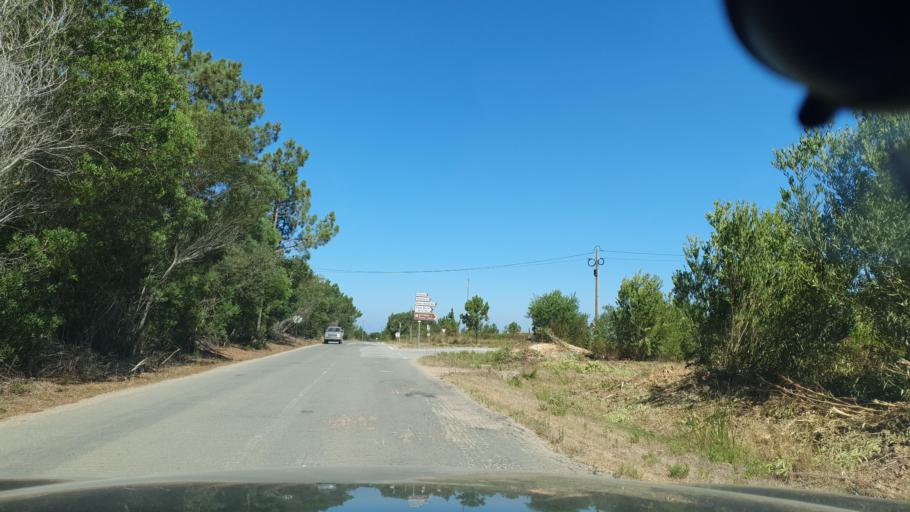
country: PT
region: Beja
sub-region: Odemira
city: Sao Teotonio
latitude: 37.5008
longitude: -8.6866
